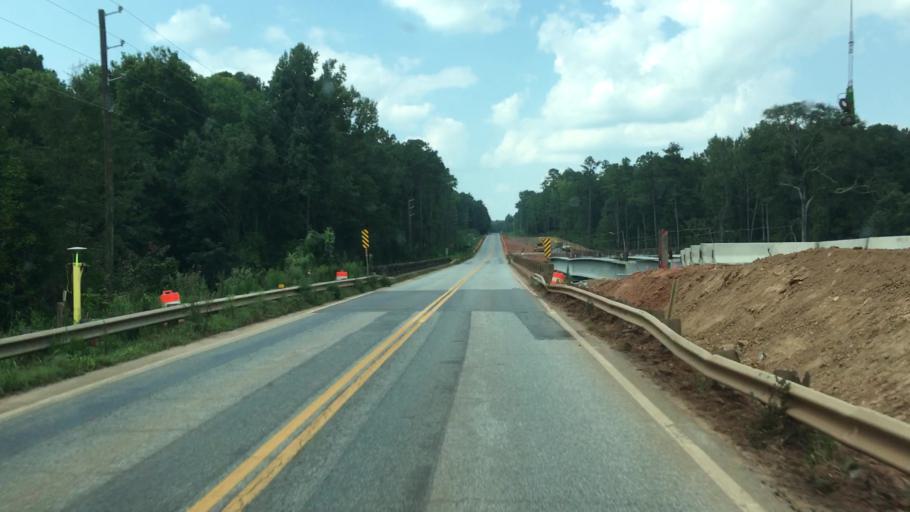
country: US
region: Georgia
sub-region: Monroe County
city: Forsyth
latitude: 33.1142
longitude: -83.8703
